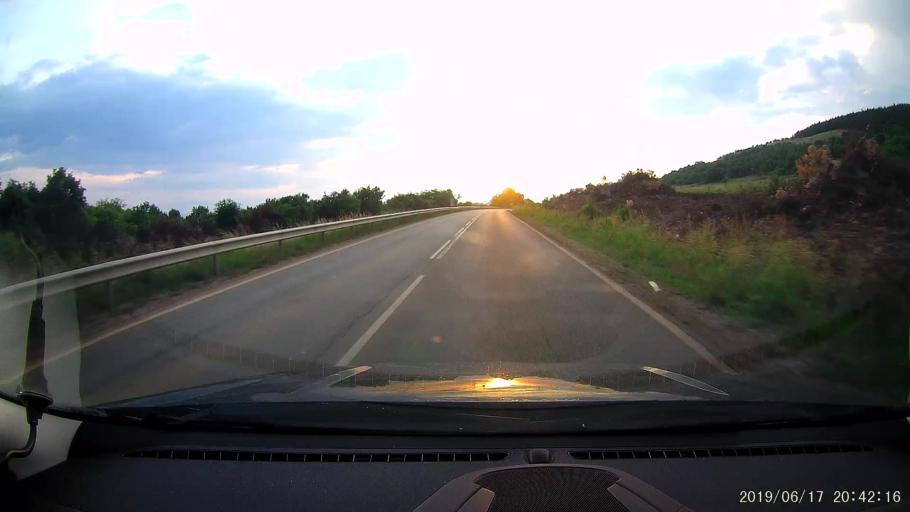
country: BG
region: Sofiya
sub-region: Obshtina Dragoman
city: Dragoman
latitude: 42.9013
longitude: 22.9527
